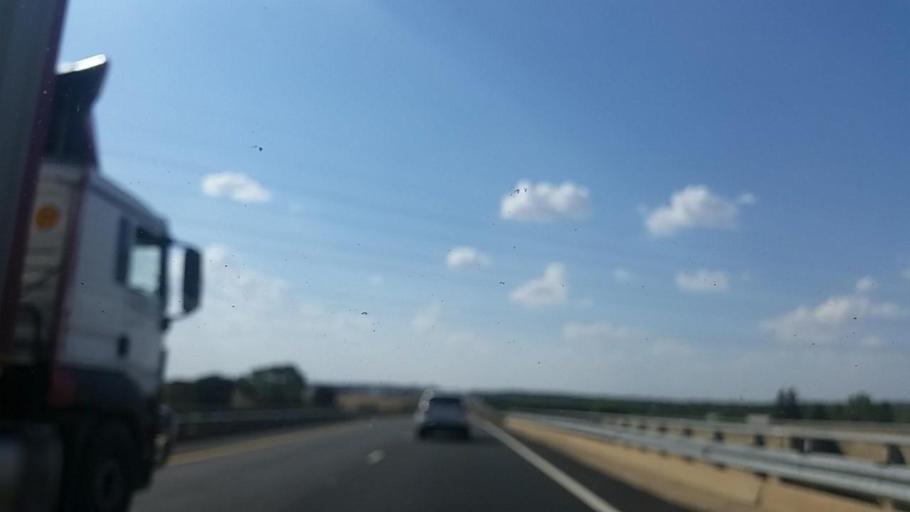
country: ZA
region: Orange Free State
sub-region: Mangaung Metropolitan Municipality
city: Bloemfontein
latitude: -29.1807
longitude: 26.1900
